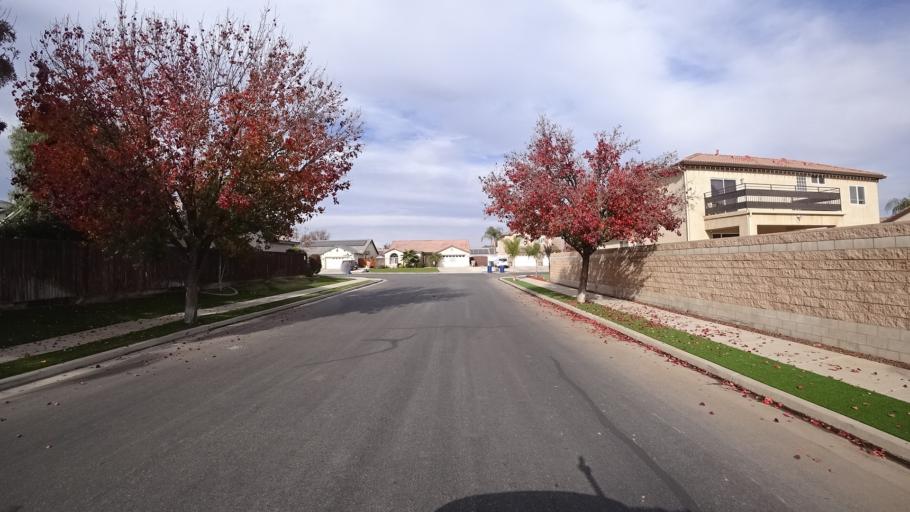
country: US
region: California
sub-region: Kern County
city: Rosedale
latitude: 35.4151
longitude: -119.1433
